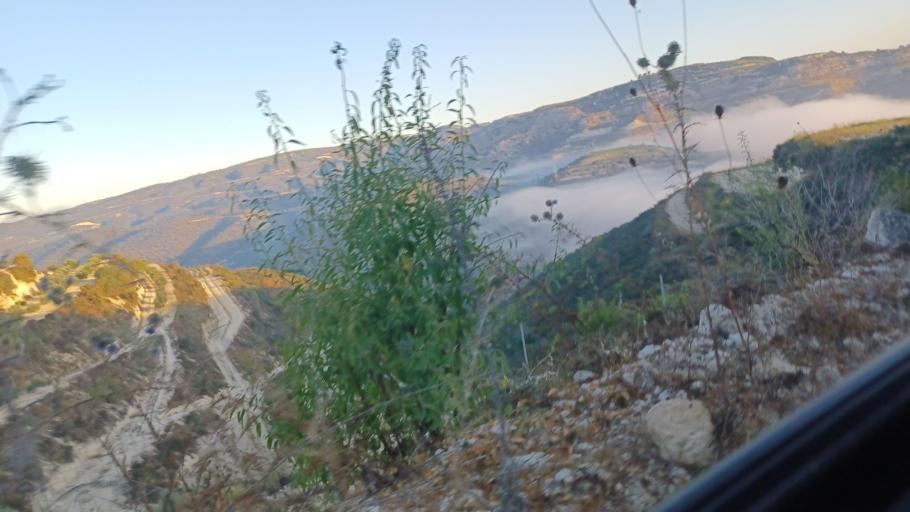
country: CY
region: Pafos
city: Tala
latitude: 34.8659
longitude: 32.4677
